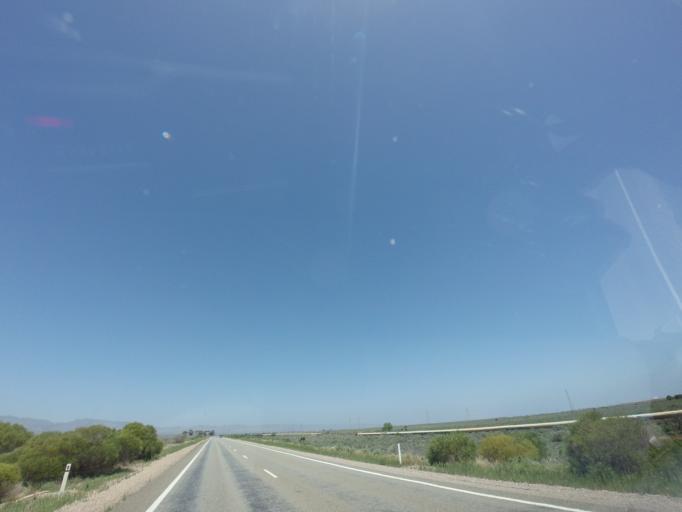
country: AU
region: South Australia
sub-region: Port Augusta
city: Port Augusta
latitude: -32.5373
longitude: 137.8485
